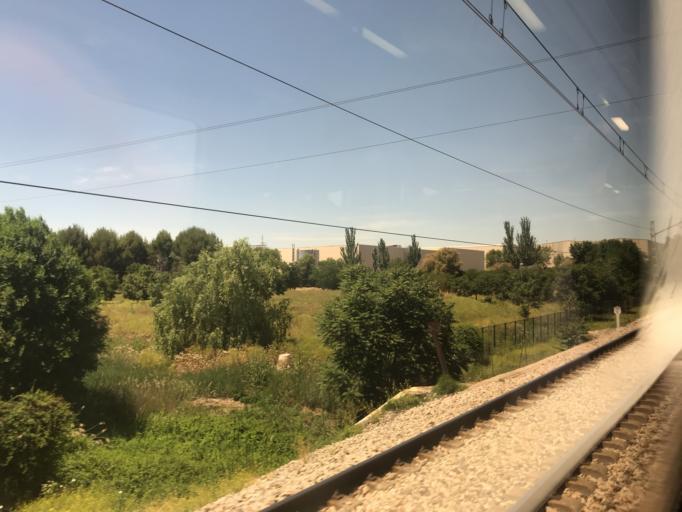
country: ES
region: Madrid
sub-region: Provincia de Madrid
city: Pinto
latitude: 40.2672
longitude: -3.7046
